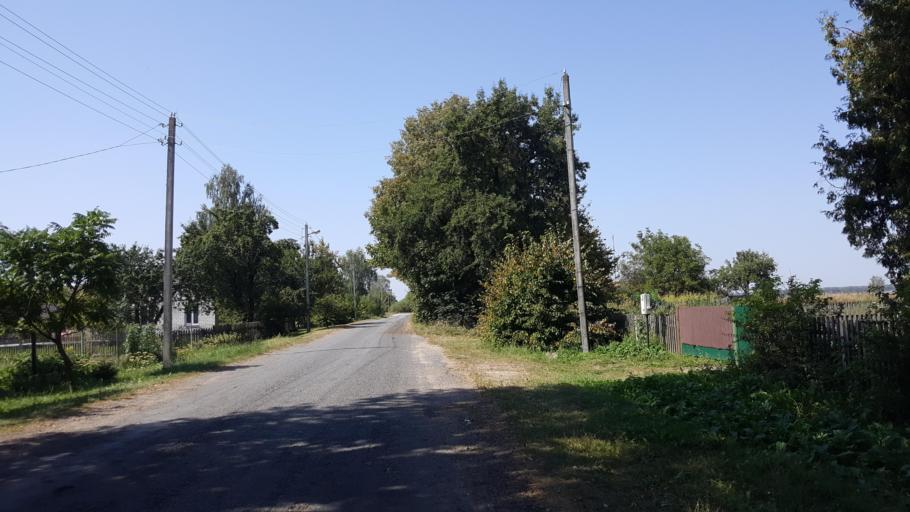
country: BY
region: Brest
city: Vysokaye
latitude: 52.4488
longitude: 23.4484
